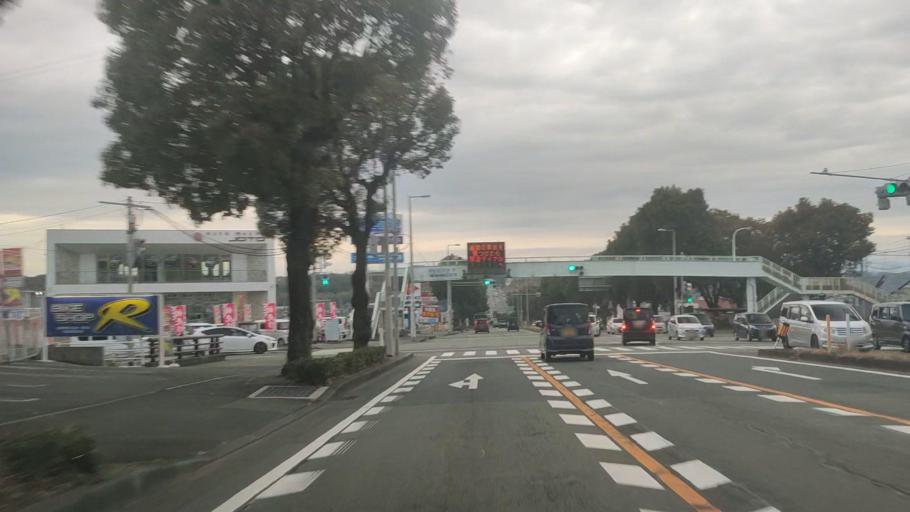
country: JP
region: Kumamoto
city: Ozu
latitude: 32.8424
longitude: 130.7806
